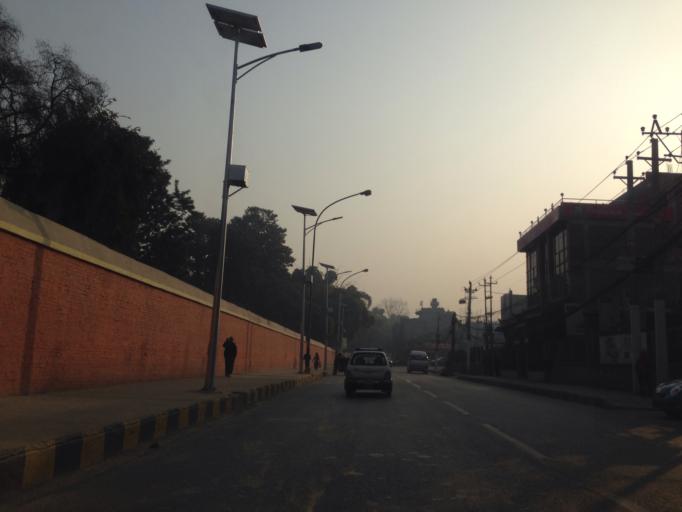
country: NP
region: Central Region
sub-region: Bagmati Zone
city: Kathmandu
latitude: 27.7137
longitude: 85.3208
